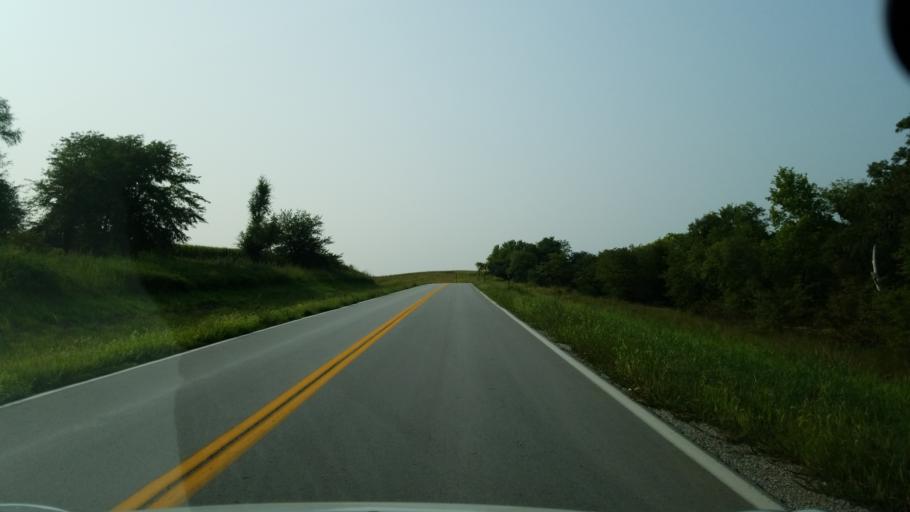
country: US
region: Nebraska
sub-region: Sarpy County
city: Offutt Air Force Base
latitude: 41.0788
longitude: -95.9303
